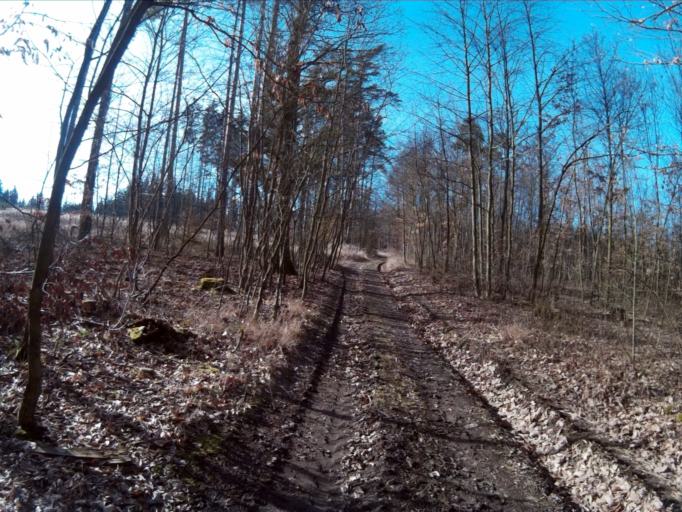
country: CZ
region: Vysocina
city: Mohelno
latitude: 49.1410
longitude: 16.1997
